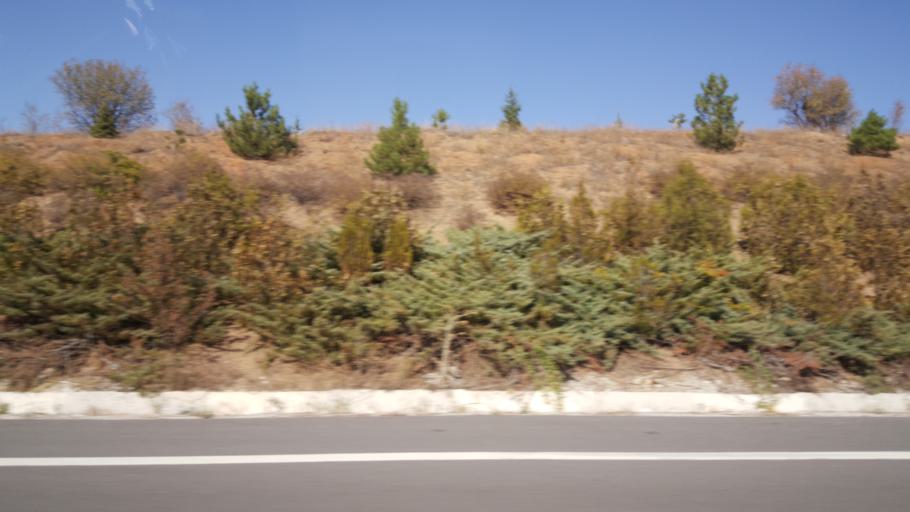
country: TR
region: Ankara
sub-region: Goelbasi
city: Golbasi
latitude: 39.8137
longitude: 32.8350
